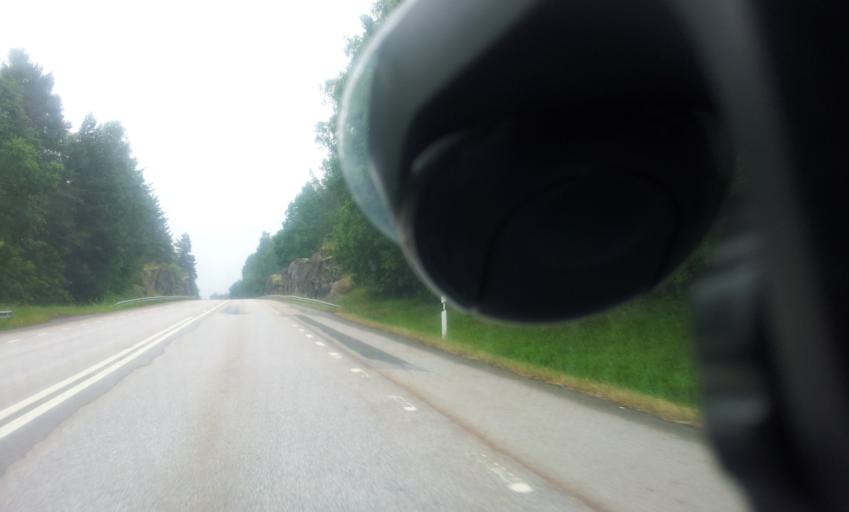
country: SE
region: Kalmar
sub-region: Vasterviks Kommun
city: Ankarsrum
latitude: 57.7079
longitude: 16.4469
